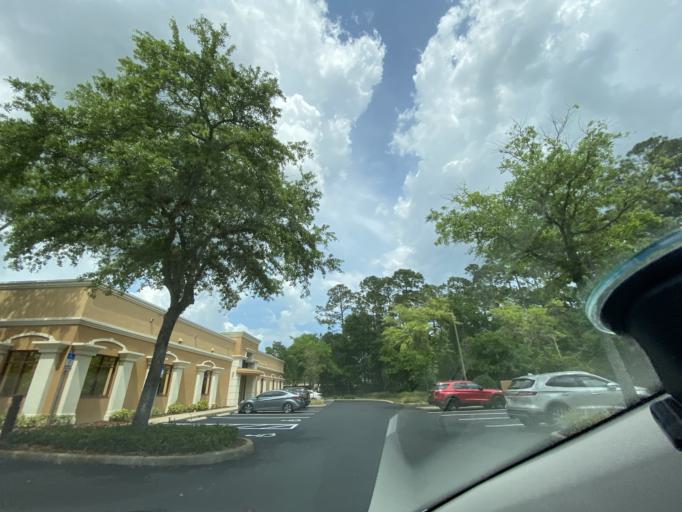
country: US
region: Florida
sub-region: Volusia County
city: Ormond Beach
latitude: 29.2676
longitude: -81.1009
